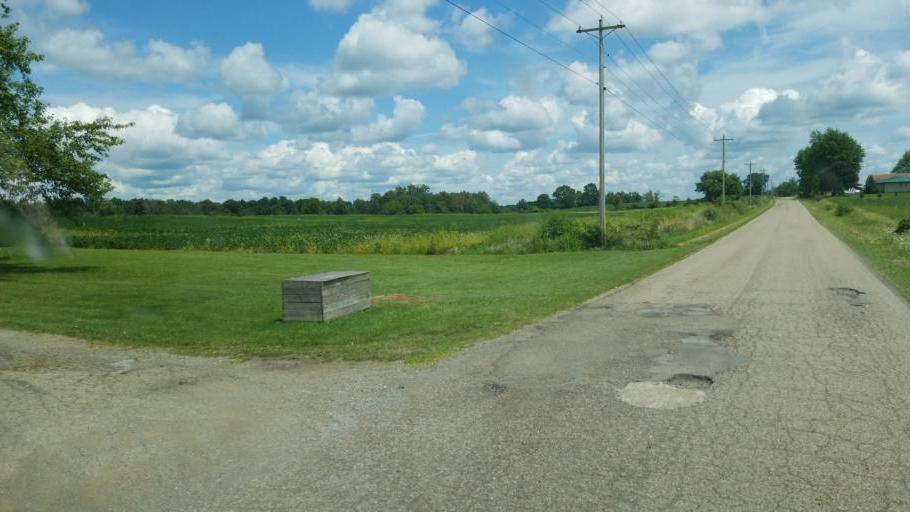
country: US
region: Ohio
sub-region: Knox County
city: Centerburg
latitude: 40.3728
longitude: -82.6917
